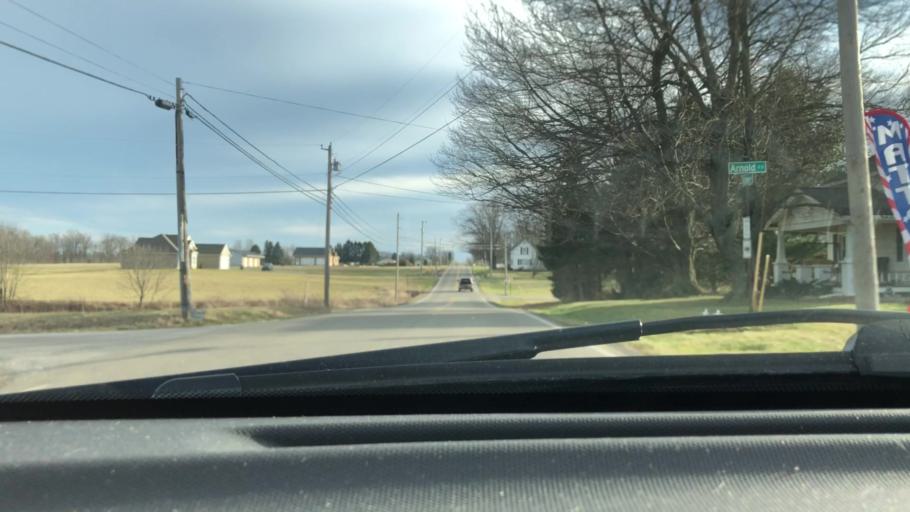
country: US
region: Ohio
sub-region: Wayne County
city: Dalton
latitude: 40.7841
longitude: -81.7454
